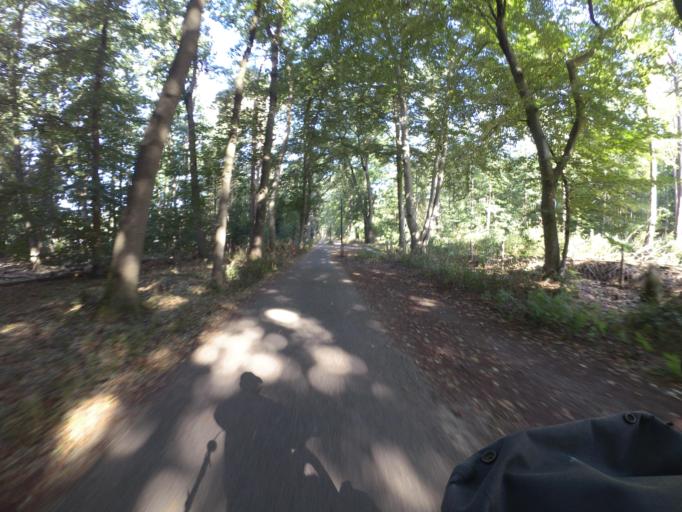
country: NL
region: Gelderland
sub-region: Gemeente Lochem
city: Lochem
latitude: 52.1464
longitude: 6.4155
